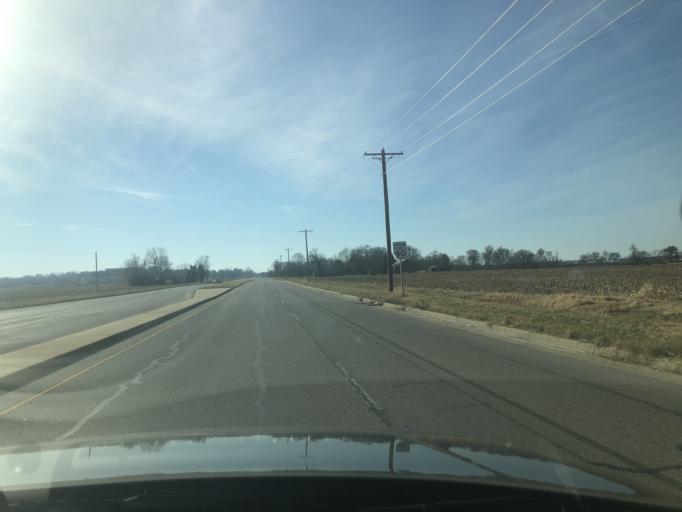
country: US
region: Indiana
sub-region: Warrick County
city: Newburgh
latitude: 37.9904
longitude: -87.4411
